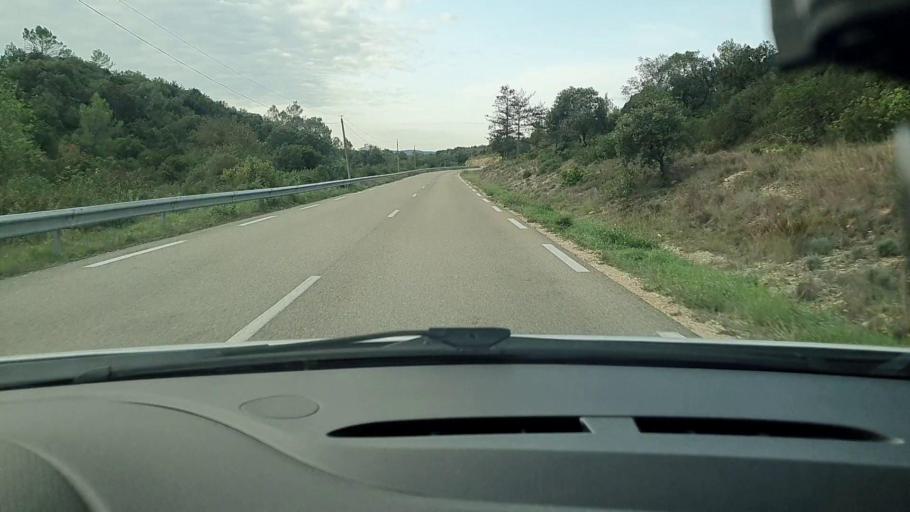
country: FR
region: Languedoc-Roussillon
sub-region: Departement du Gard
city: Mons
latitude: 44.0947
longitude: 4.2211
